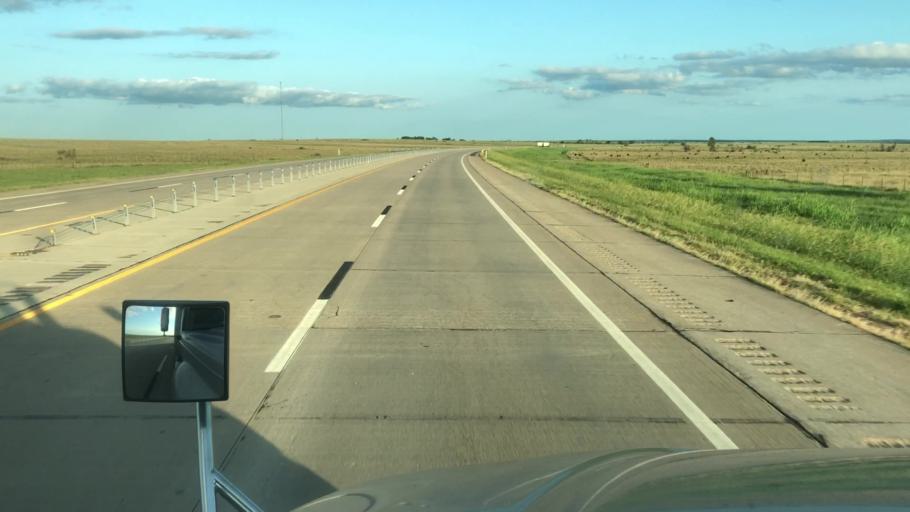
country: US
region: Oklahoma
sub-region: Pawnee County
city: Pawnee
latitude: 36.3748
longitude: -97.0413
